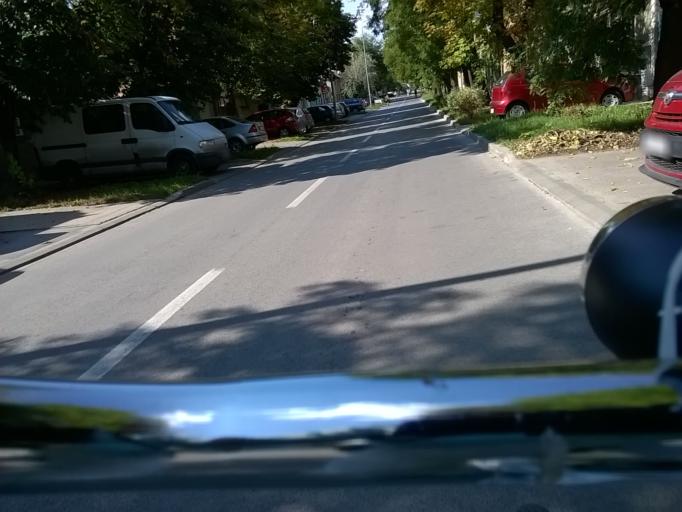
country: RS
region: Autonomna Pokrajina Vojvodina
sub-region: Juznobanatski Okrug
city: Pancevo
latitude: 44.8748
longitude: 20.6410
